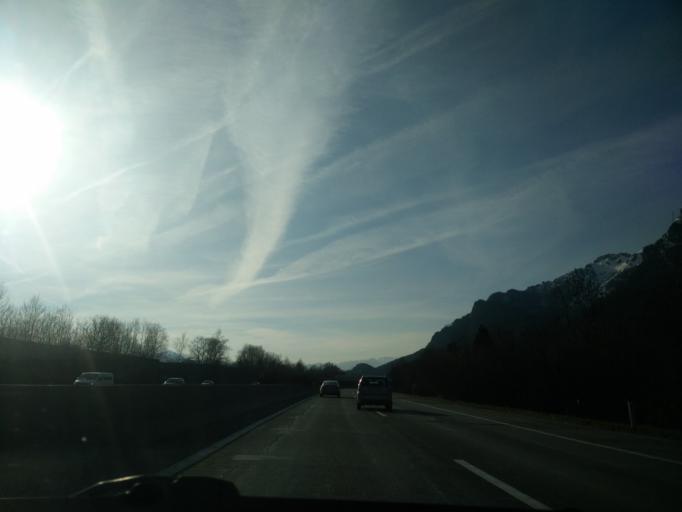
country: AT
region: Salzburg
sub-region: Politischer Bezirk Salzburg-Umgebung
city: Grodig
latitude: 47.7639
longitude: 12.9983
